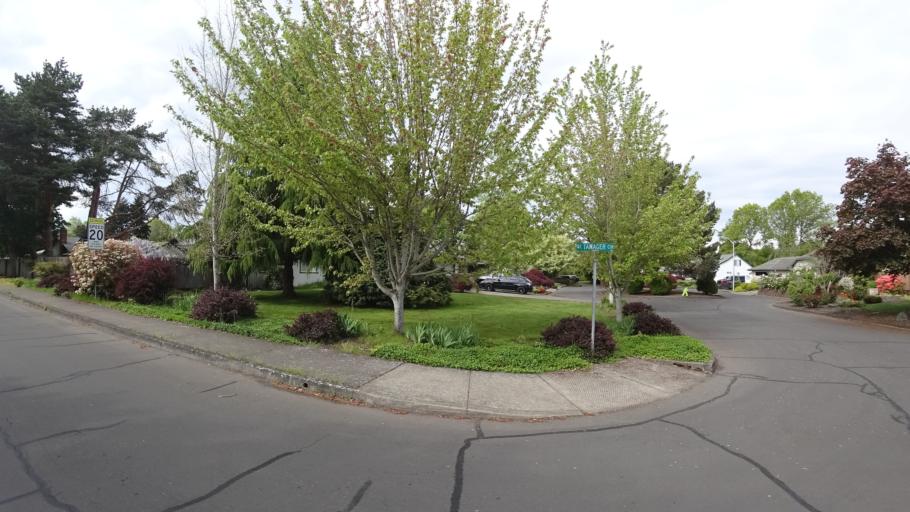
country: US
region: Oregon
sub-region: Washington County
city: Hillsboro
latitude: 45.4987
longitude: -122.9622
